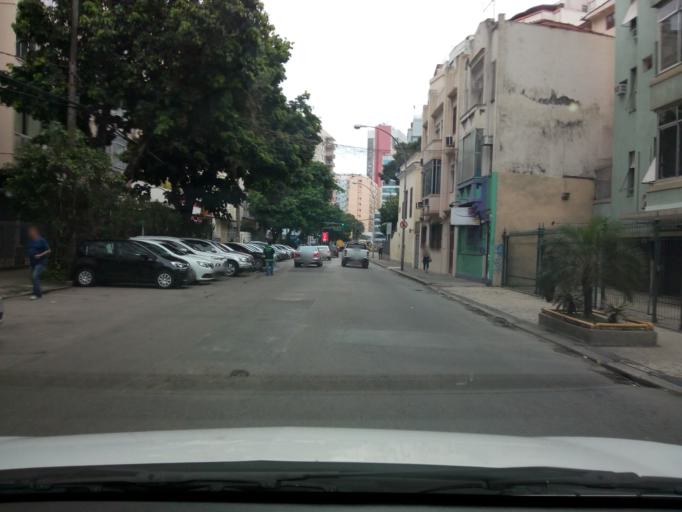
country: BR
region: Rio de Janeiro
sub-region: Rio De Janeiro
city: Rio de Janeiro
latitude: -22.9331
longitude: -43.1802
